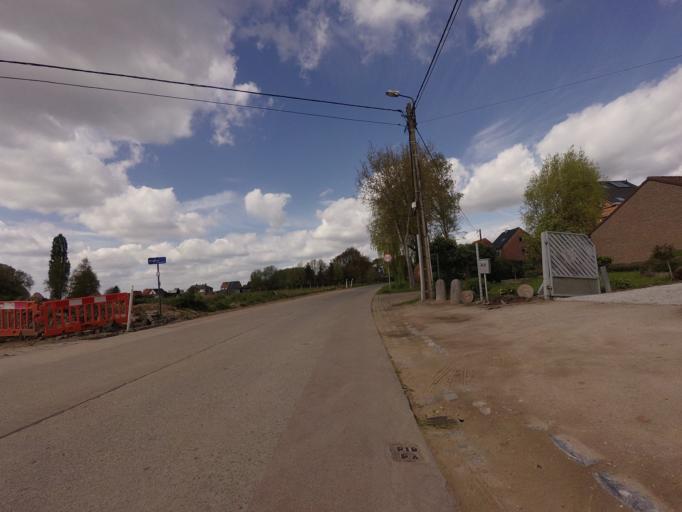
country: BE
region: Flanders
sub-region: Provincie Vlaams-Brabant
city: Kapelle-op-den-Bos
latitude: 51.0156
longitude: 4.4161
